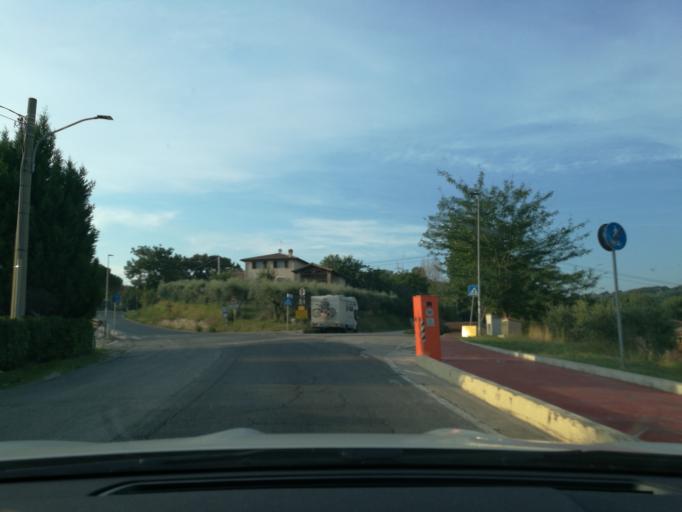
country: IT
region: Umbria
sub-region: Provincia di Terni
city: San Gemini
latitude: 42.6227
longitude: 12.5492
